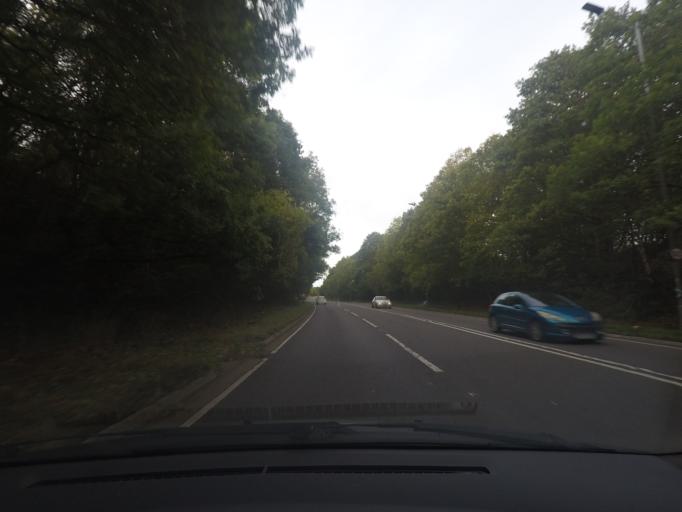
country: GB
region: England
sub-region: Sheffield
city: Chapletown
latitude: 53.4823
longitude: -1.4951
